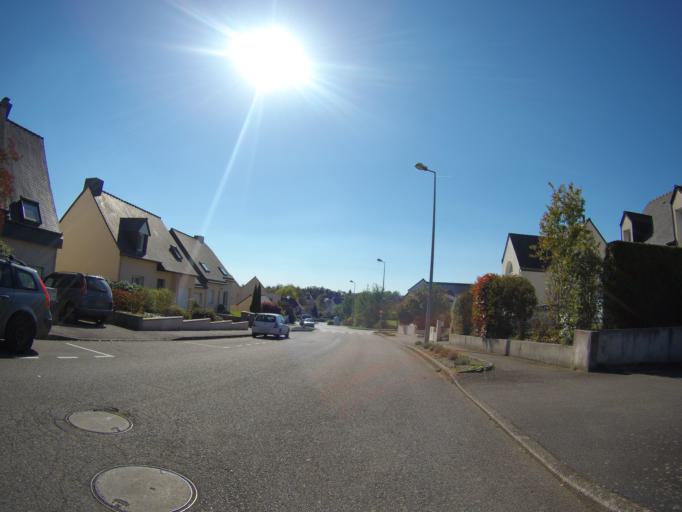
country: FR
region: Brittany
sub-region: Departement d'Ille-et-Vilaine
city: Vern-sur-Seiche
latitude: 48.0469
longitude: -1.6134
